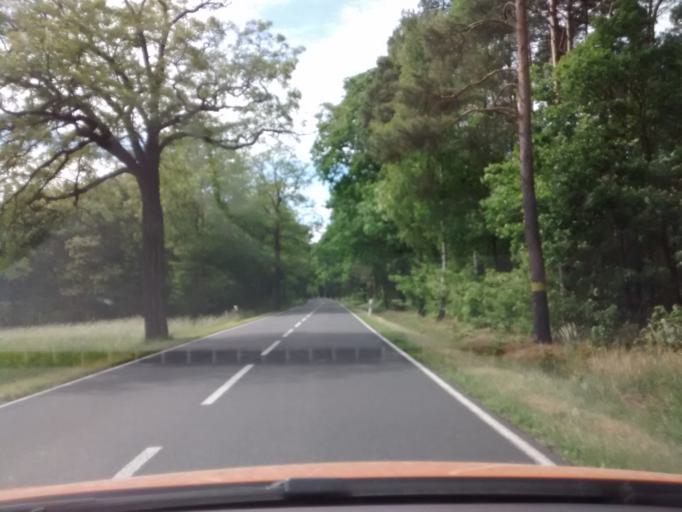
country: DE
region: Brandenburg
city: Ihlow
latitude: 51.9870
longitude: 13.2886
